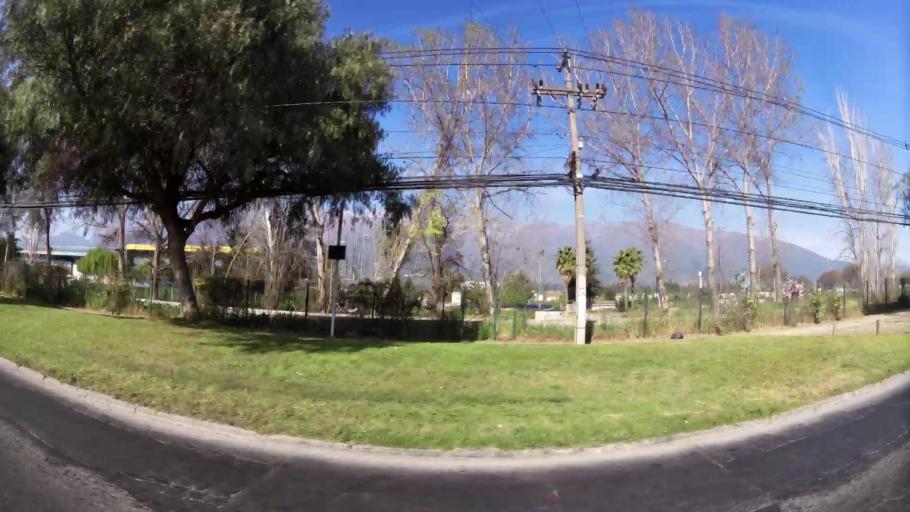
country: CL
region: Santiago Metropolitan
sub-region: Provincia de Santiago
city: Villa Presidente Frei, Nunoa, Santiago, Chile
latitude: -33.4921
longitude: -70.5592
